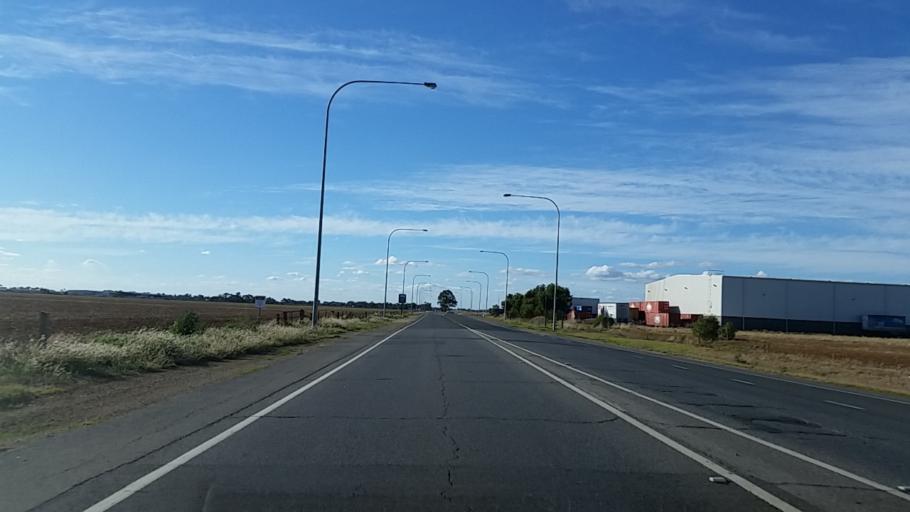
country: AU
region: South Australia
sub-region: Salisbury
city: Salisbury
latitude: -34.7192
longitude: 138.5990
